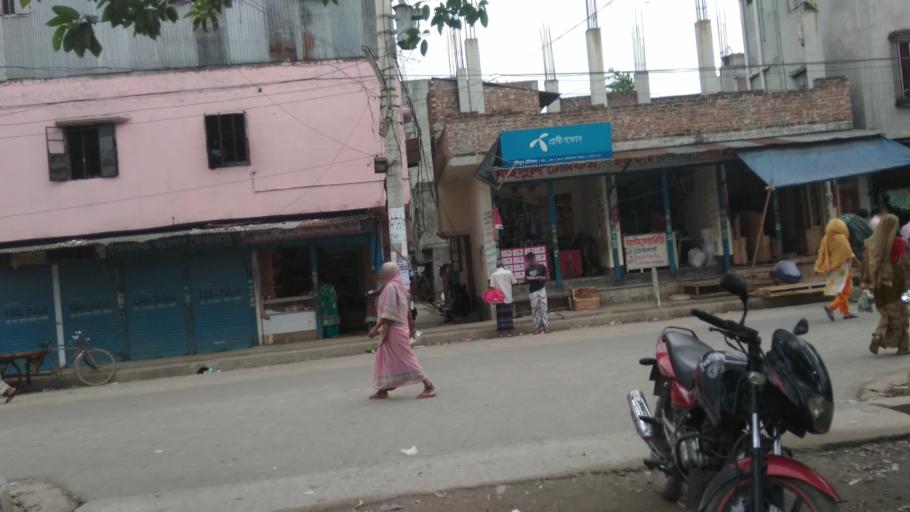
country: BD
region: Dhaka
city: Tungi
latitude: 23.8197
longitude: 90.3805
